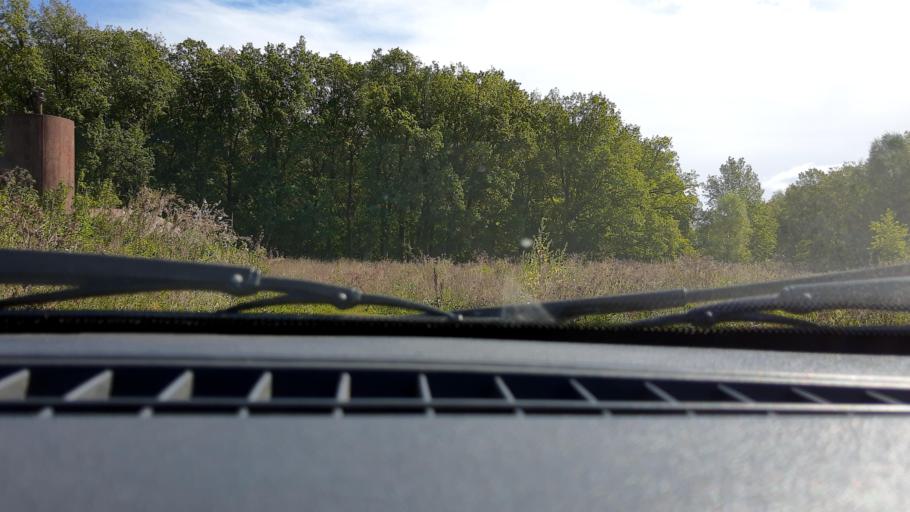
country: RU
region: Bashkortostan
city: Mikhaylovka
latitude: 54.8224
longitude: 55.7917
